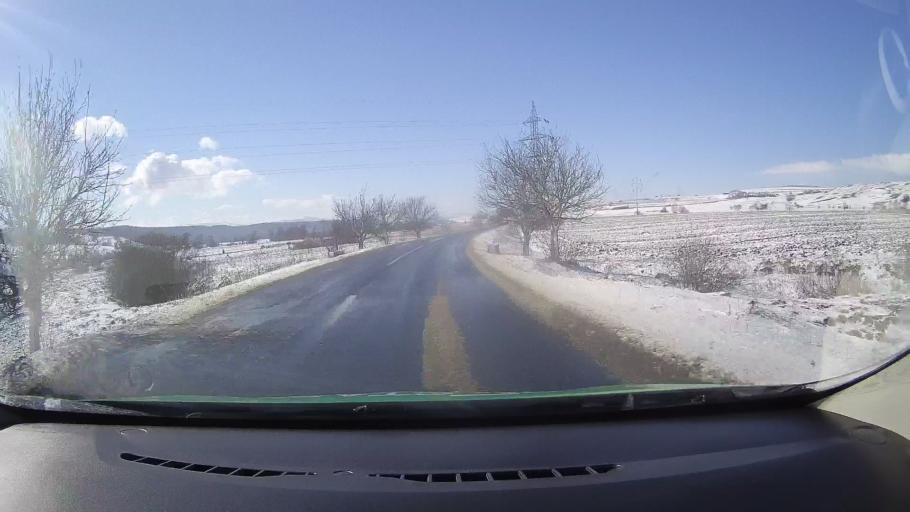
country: RO
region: Sibiu
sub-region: Comuna Rosia
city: Rosia
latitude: 45.7939
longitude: 24.3300
